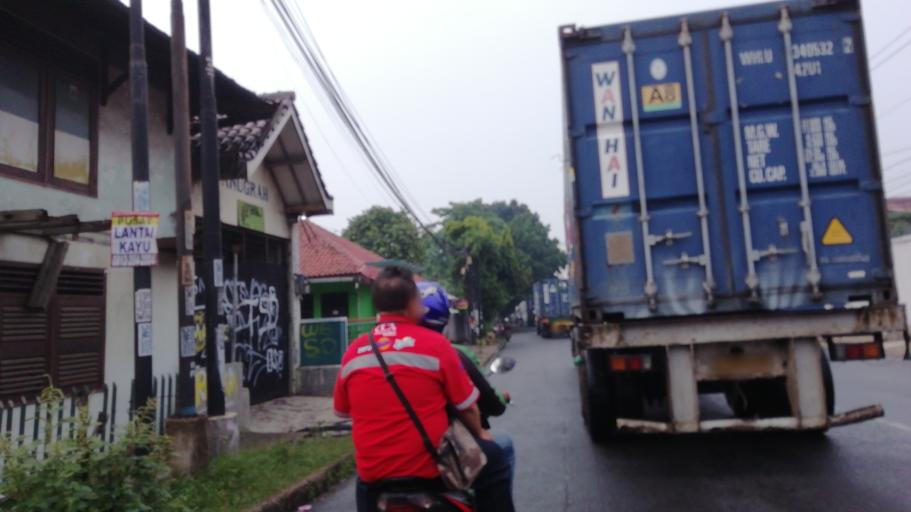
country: ID
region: West Java
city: Bogor
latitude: -6.5435
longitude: 106.8058
